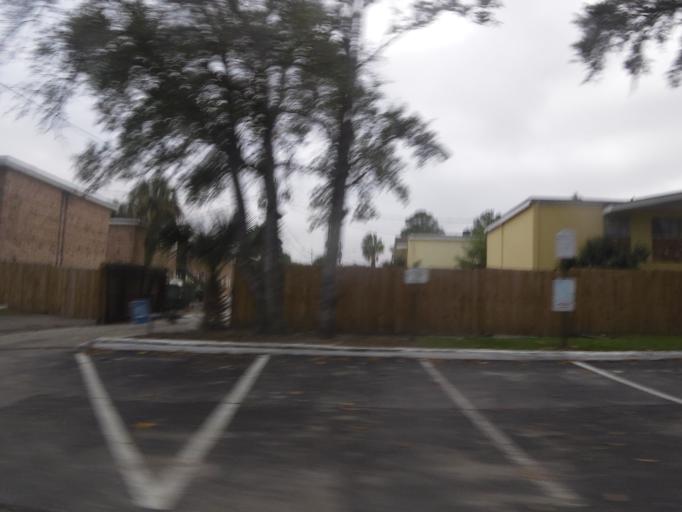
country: US
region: Florida
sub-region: Clay County
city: Bellair-Meadowbrook Terrace
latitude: 30.2802
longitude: -81.7456
